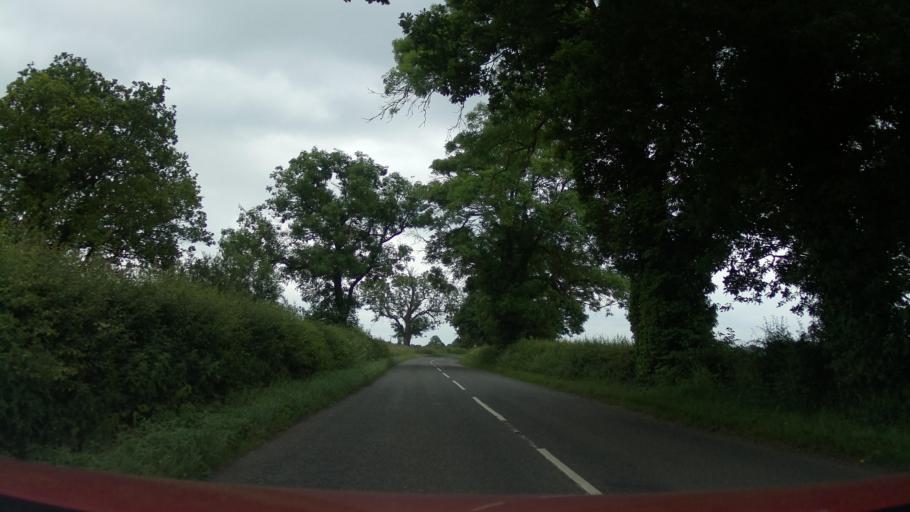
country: GB
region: England
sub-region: Derbyshire
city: Rodsley
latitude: 52.8740
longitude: -1.7313
